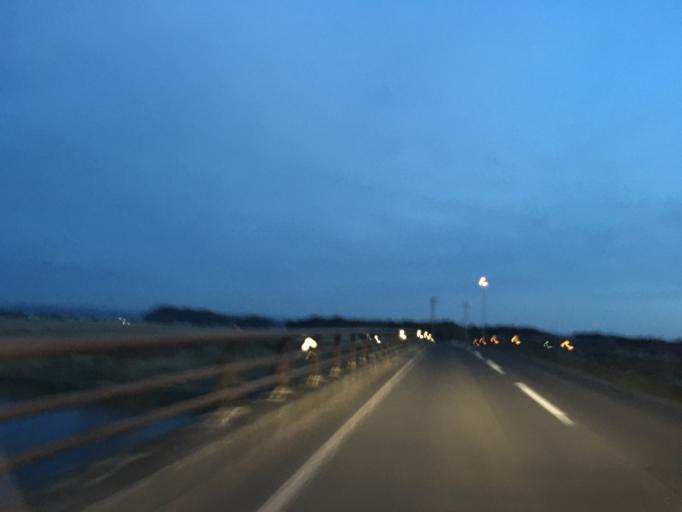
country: JP
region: Miyagi
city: Wakuya
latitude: 38.7121
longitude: 141.1475
